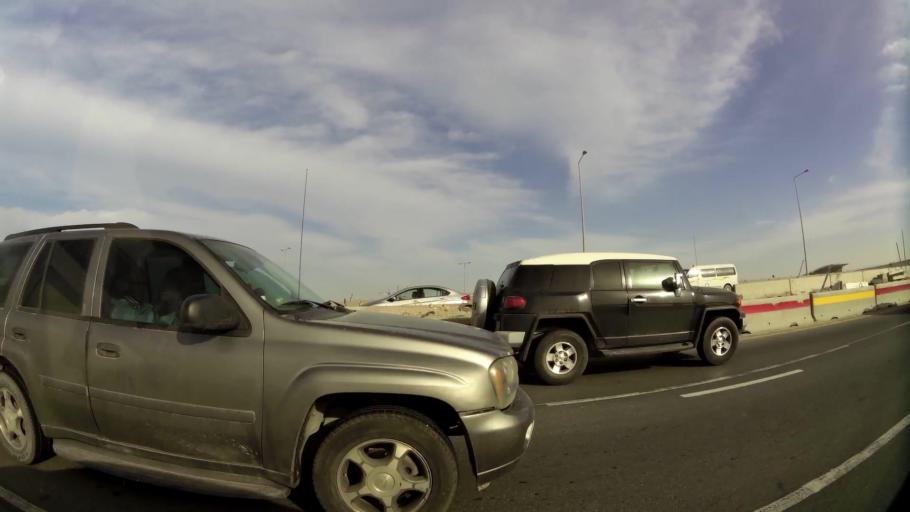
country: QA
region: Al Wakrah
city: Al Wakrah
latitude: 25.2159
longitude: 51.5853
